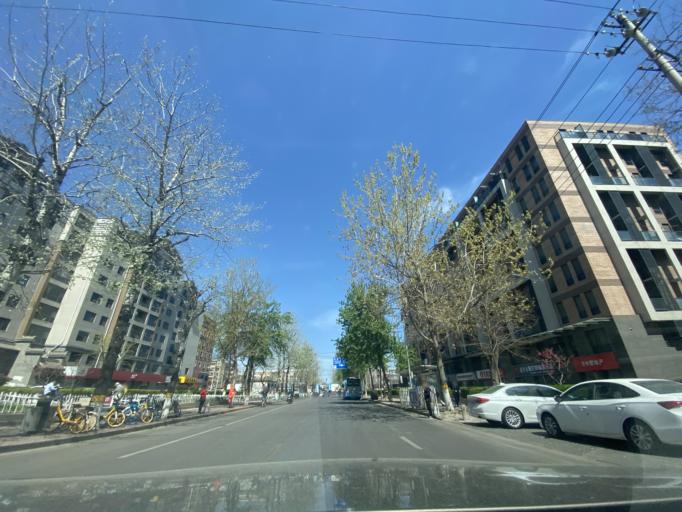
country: CN
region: Beijing
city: Sijiqing
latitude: 39.9263
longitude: 116.2588
